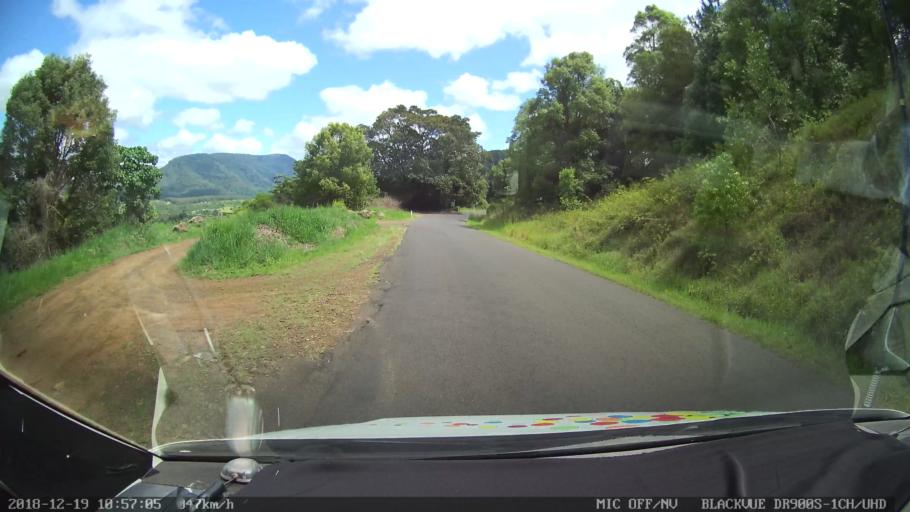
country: AU
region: New South Wales
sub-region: Lismore Municipality
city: Nimbin
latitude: -28.5899
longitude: 153.2613
